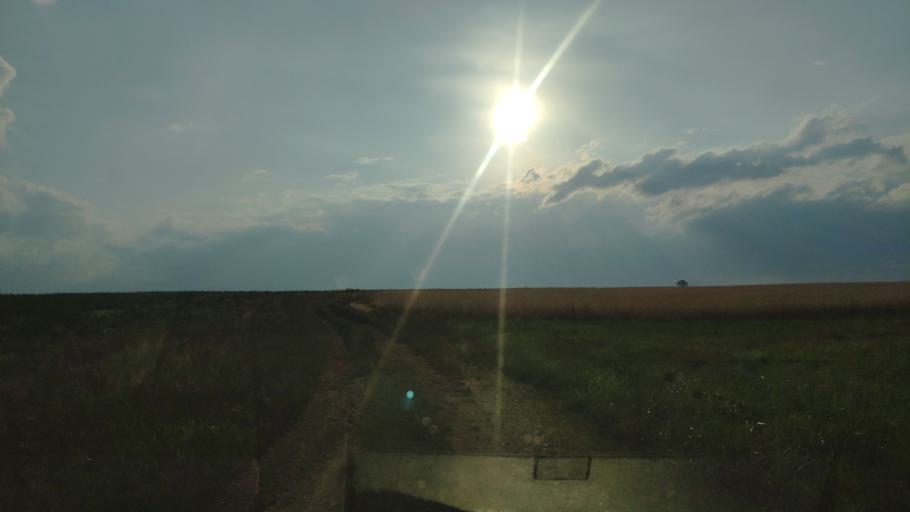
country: SK
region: Kosicky
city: Moldava nad Bodvou
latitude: 48.6933
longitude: 21.0004
